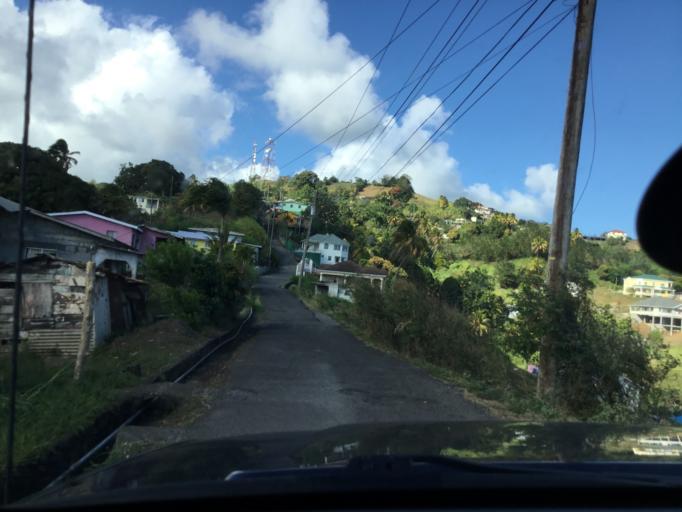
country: VC
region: Saint George
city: Kingstown
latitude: 13.1580
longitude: -61.1776
